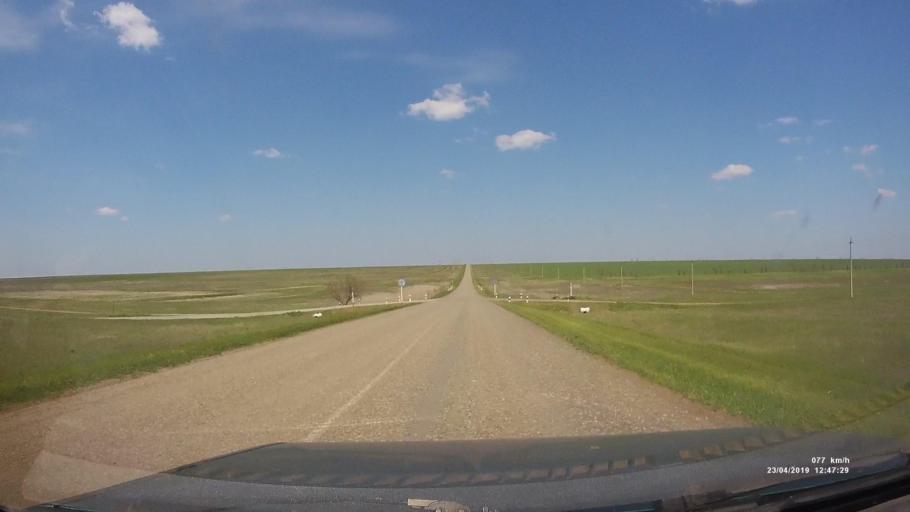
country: RU
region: Kalmykiya
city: Yashalta
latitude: 46.5123
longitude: 42.6388
